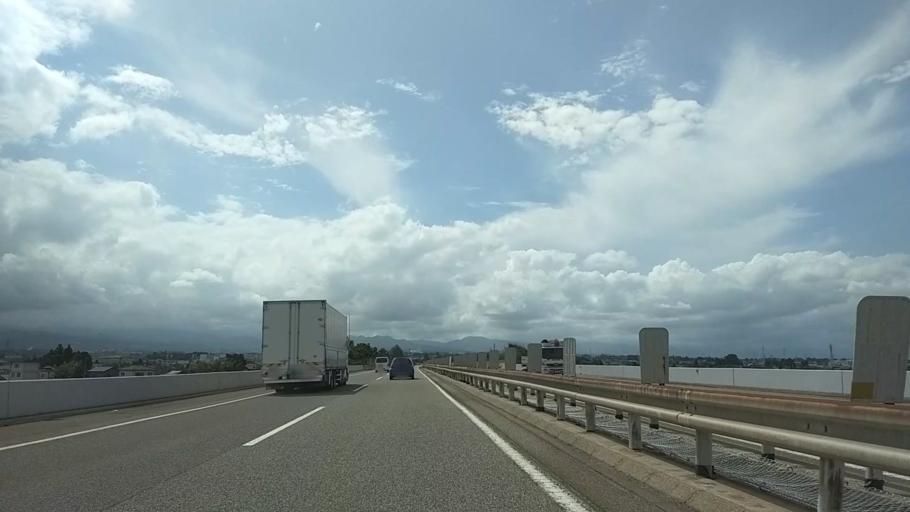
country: JP
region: Toyama
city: Kamiichi
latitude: 36.6993
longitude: 137.3327
